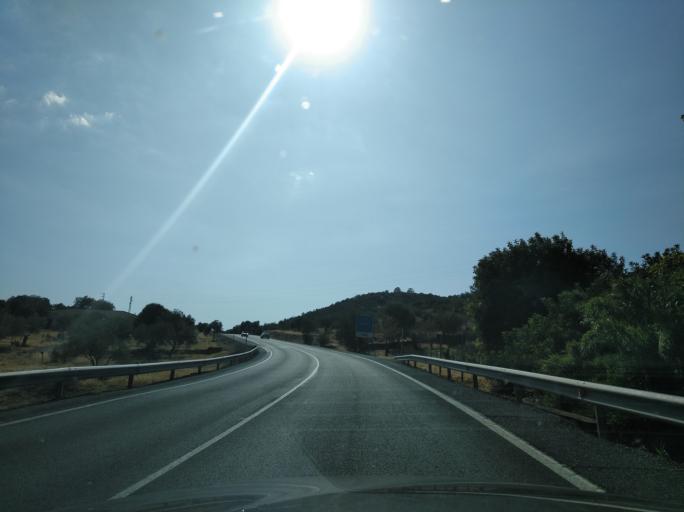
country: ES
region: Andalusia
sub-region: Provincia de Huelva
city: Rosal de la Frontera
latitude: 37.9654
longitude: -7.2340
